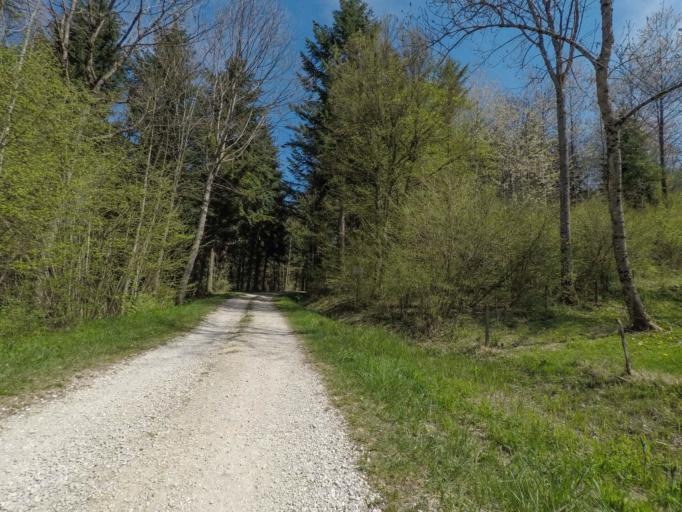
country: FR
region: Rhone-Alpes
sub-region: Departement de la Haute-Savoie
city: Archamps
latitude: 46.1159
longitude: 6.1415
